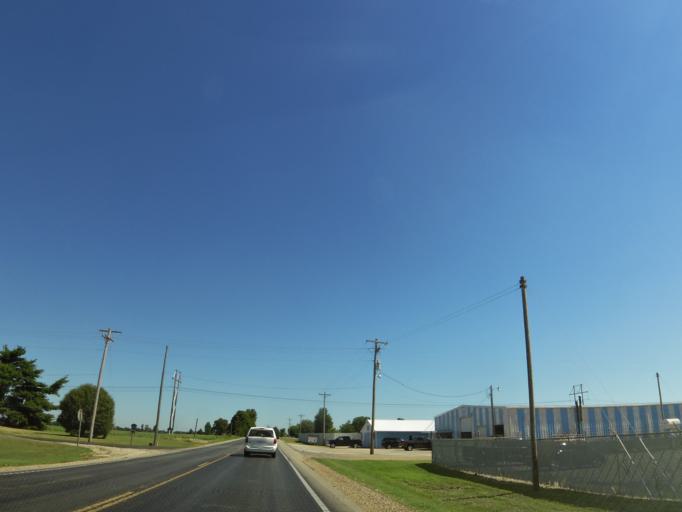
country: US
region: Missouri
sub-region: Dunklin County
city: Malden
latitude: 36.5196
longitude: -89.9714
